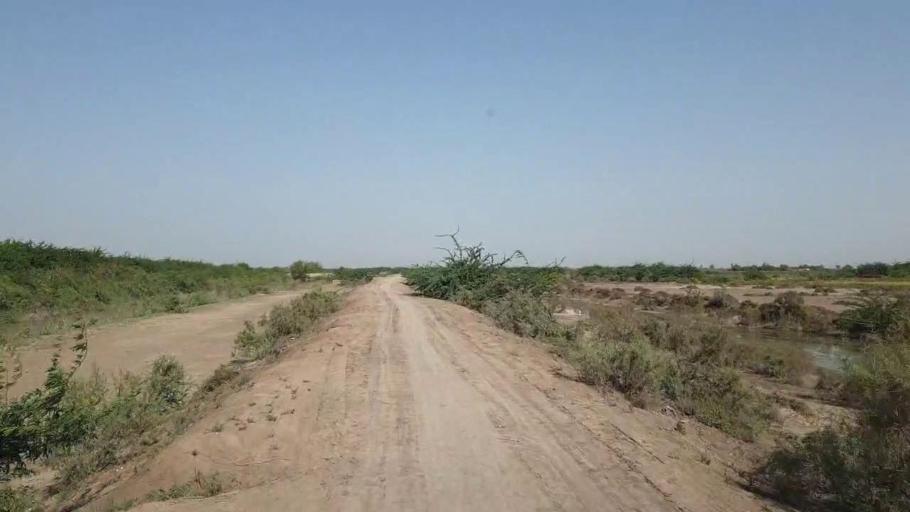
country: PK
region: Sindh
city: Tando Bago
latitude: 24.6545
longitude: 69.0705
